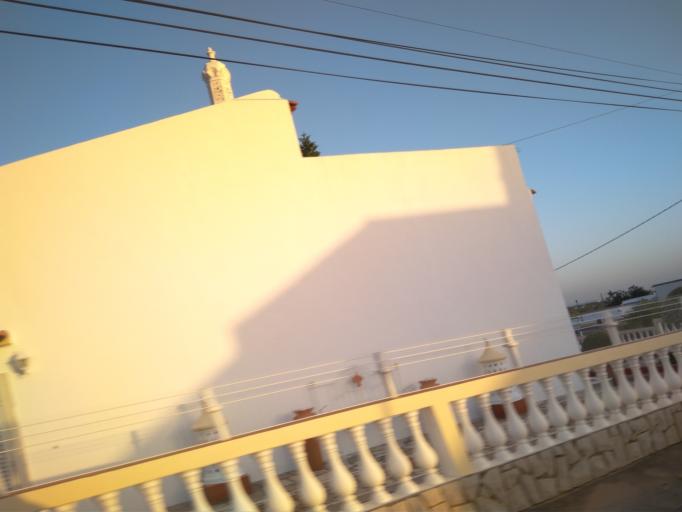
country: PT
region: Faro
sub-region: Faro
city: Santa Barbara de Nexe
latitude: 37.0836
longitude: -7.9586
